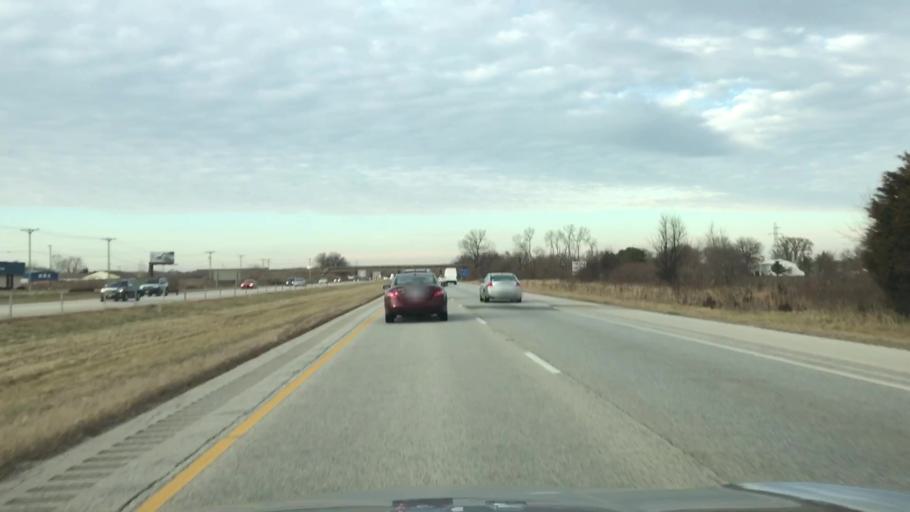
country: US
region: Illinois
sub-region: Sangamon County
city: Grandview
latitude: 39.8420
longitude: -89.5939
